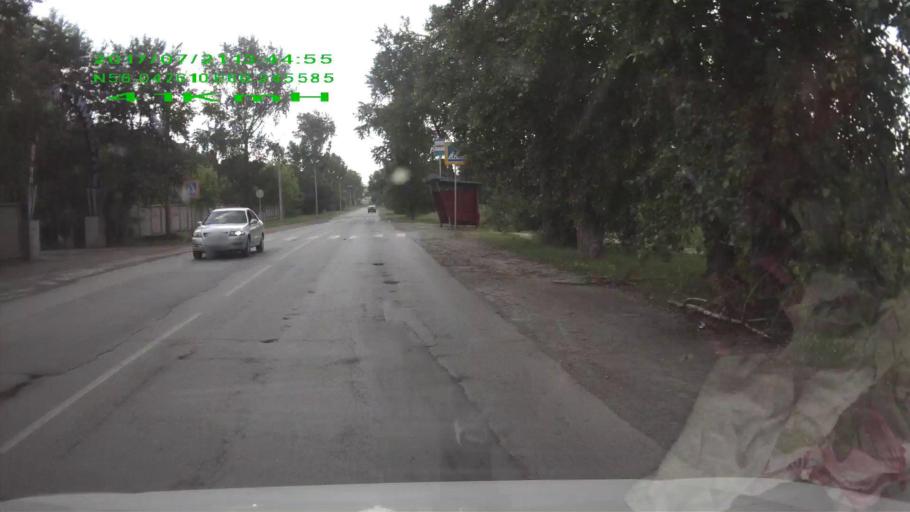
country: RU
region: Chelyabinsk
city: Verkhniy Ufaley
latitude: 56.0471
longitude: 60.2455
